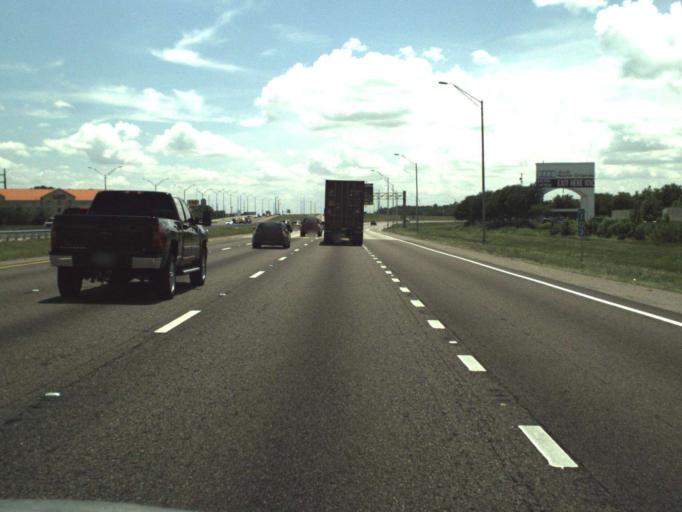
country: US
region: Florida
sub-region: Seminole County
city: Lake Mary
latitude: 28.8186
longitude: -81.3346
